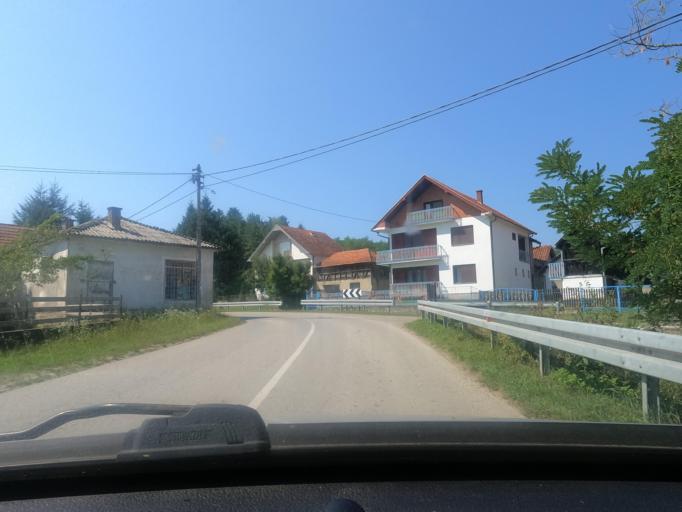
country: RS
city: Jadranska Lesnica
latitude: 44.5474
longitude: 19.3535
